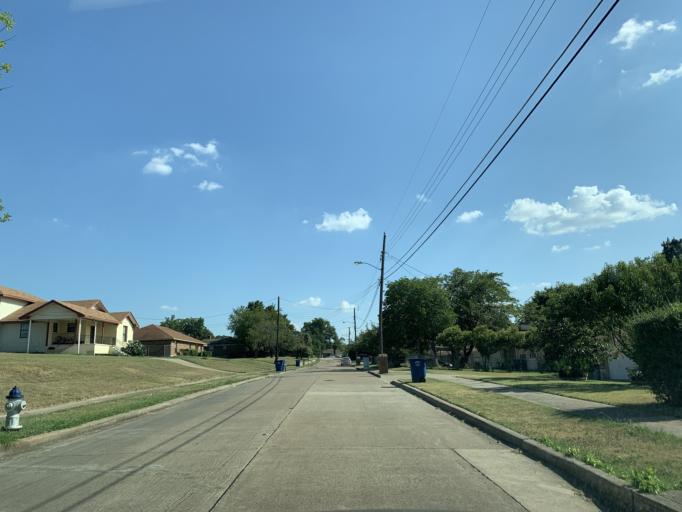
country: US
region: Texas
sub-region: Dallas County
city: Hutchins
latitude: 32.6568
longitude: -96.7798
